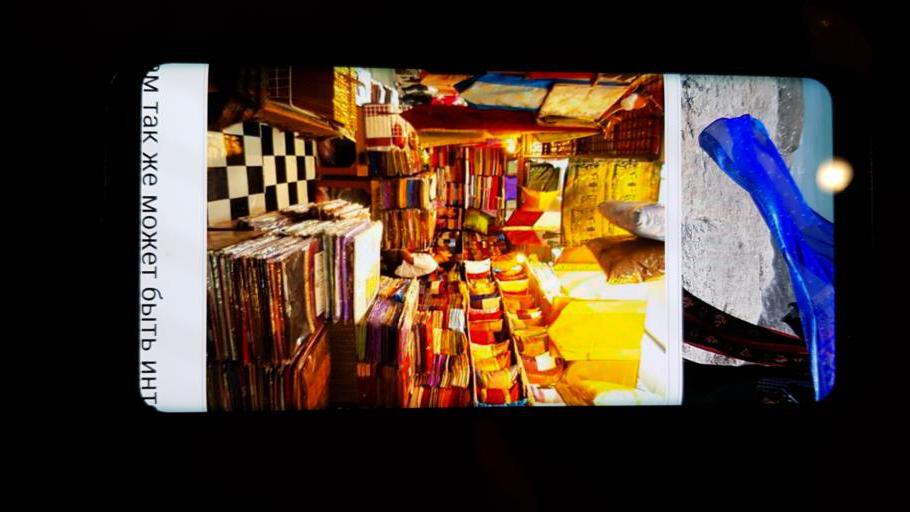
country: TH
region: Trat
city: Laem Ngop
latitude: 12.1059
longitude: 102.2763
